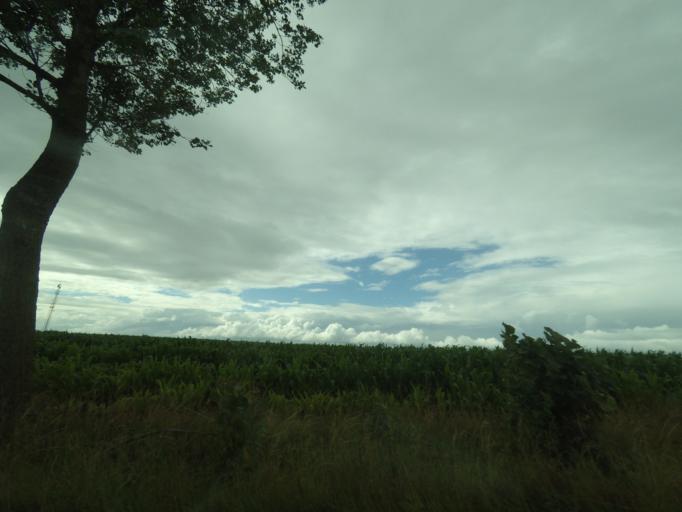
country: DK
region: South Denmark
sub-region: Nordfyns Kommune
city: Sonderso
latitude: 55.4927
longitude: 10.2379
